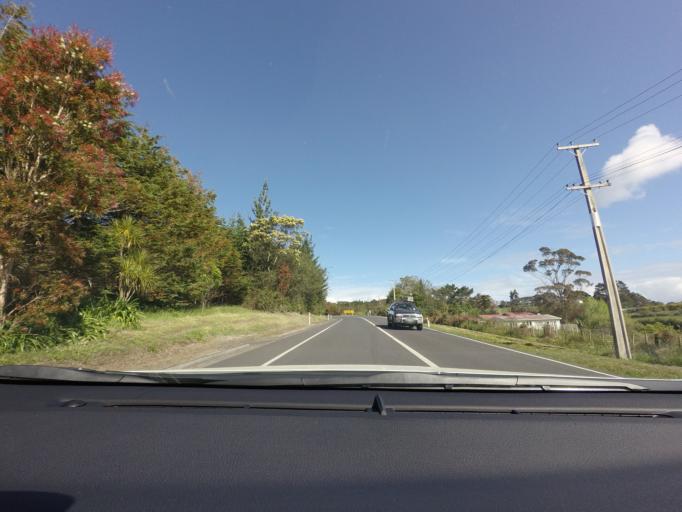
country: NZ
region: Auckland
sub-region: Auckland
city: Rothesay Bay
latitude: -36.7134
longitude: 174.6500
